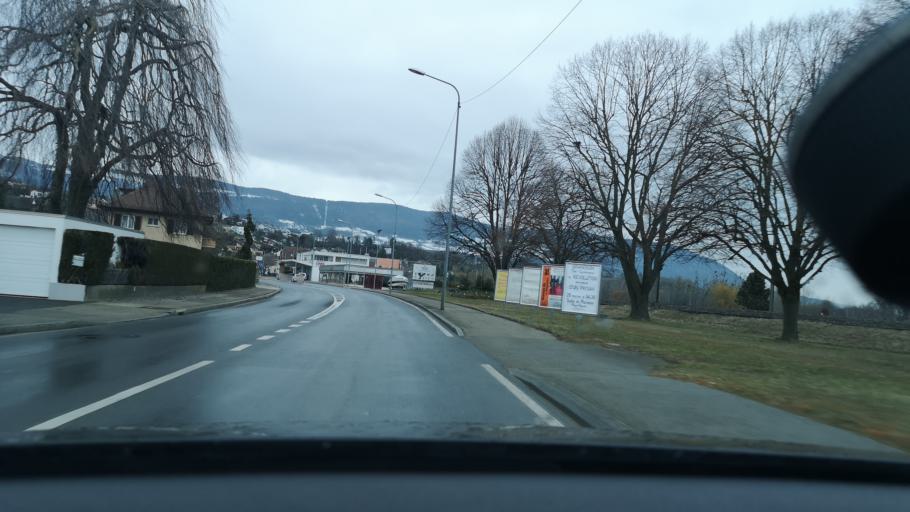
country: CH
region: Vaud
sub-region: Jura-Nord vaudois District
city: Montagny
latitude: 46.7951
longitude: 6.6283
